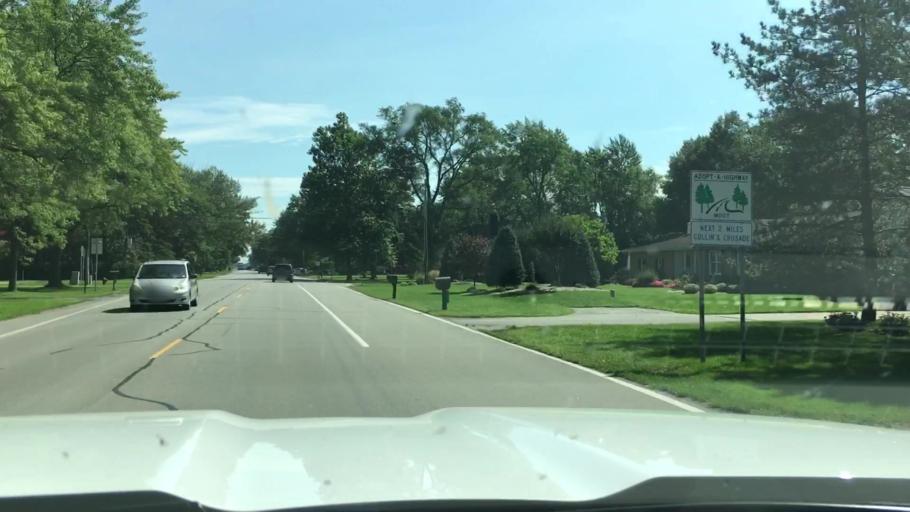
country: US
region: Michigan
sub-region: Bay County
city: Essexville
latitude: 43.5940
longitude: -83.8179
